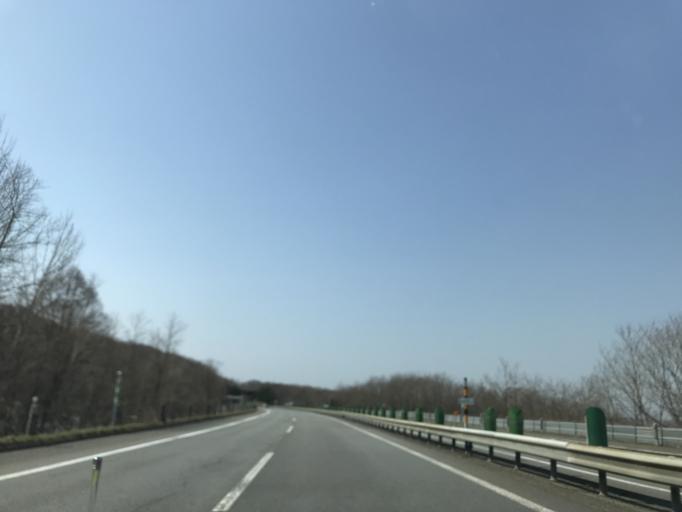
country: JP
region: Hokkaido
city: Bibai
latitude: 43.2944
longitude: 141.8678
